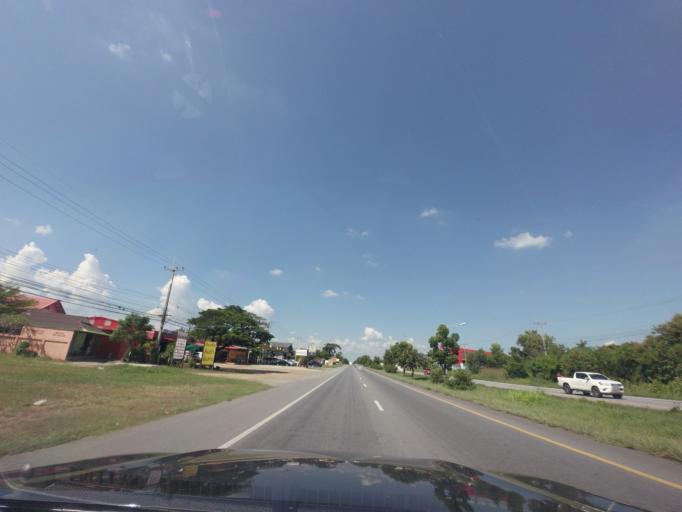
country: TH
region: Nakhon Ratchasima
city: Non Sung
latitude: 15.1517
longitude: 102.3268
